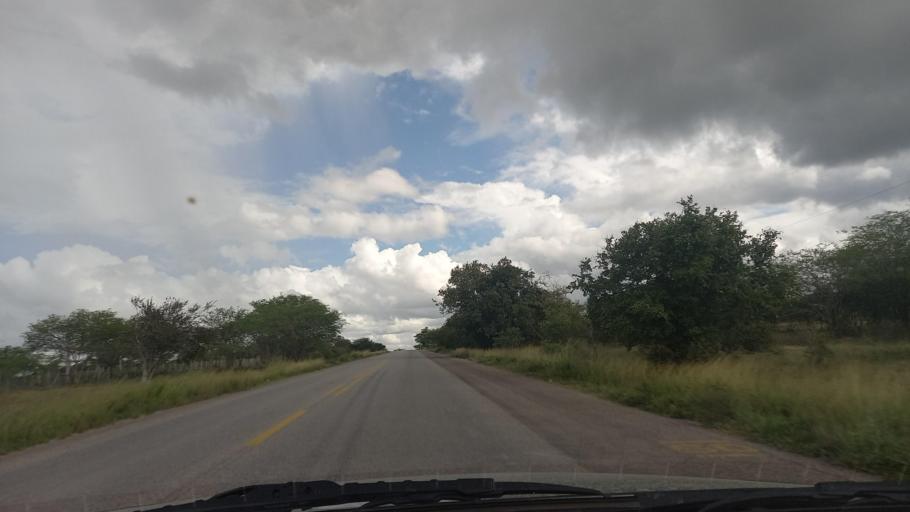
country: BR
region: Pernambuco
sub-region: Cachoeirinha
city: Cachoeirinha
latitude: -8.5335
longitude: -36.2650
